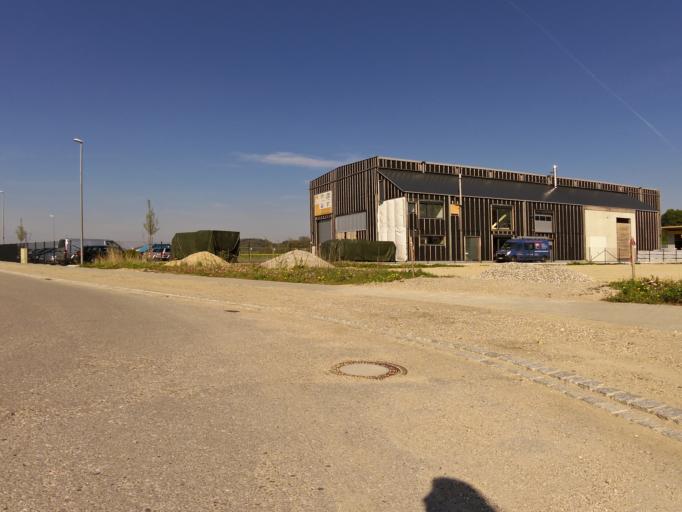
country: DE
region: Bavaria
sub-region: Upper Bavaria
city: Langenpreising
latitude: 48.4318
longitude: 11.9797
